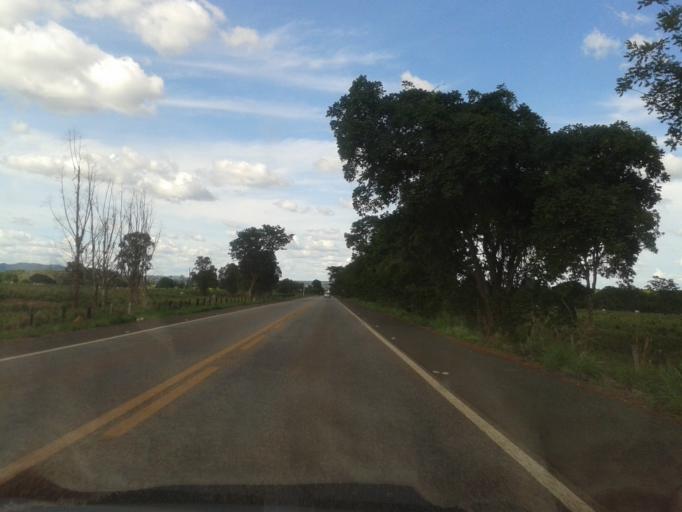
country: BR
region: Goias
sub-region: Mozarlandia
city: Mozarlandia
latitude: -15.0275
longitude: -50.5998
